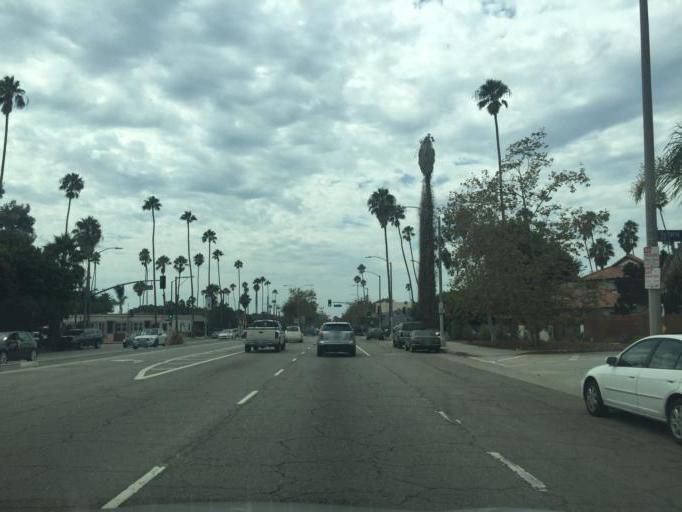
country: US
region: California
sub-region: Los Angeles County
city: Marina del Rey
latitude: 33.9924
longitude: -118.4563
